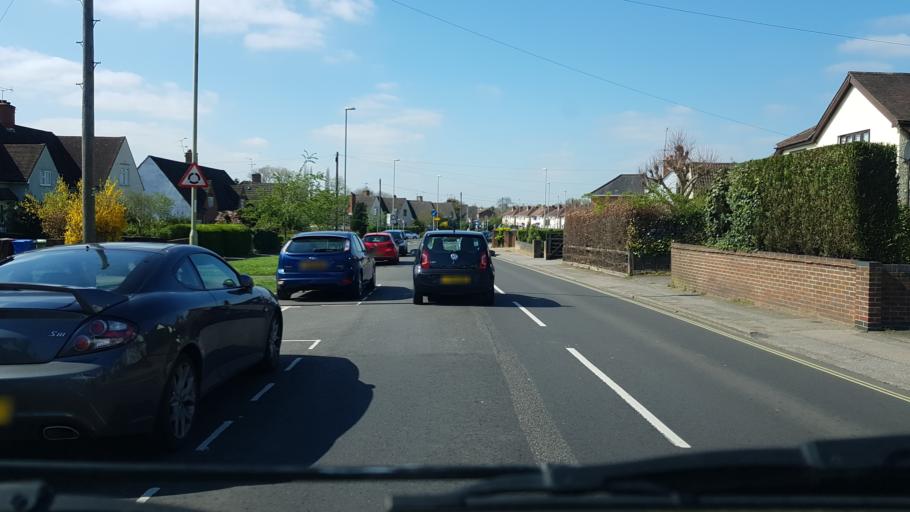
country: GB
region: England
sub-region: Hampshire
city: Aldershot
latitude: 51.2358
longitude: -0.7552
